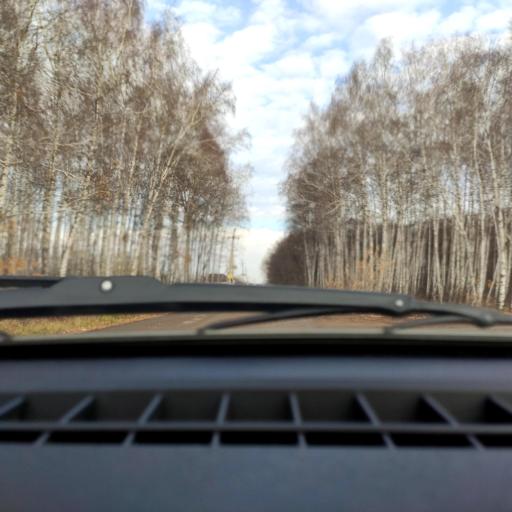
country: RU
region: Bashkortostan
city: Ufa
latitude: 54.6277
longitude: 55.8903
